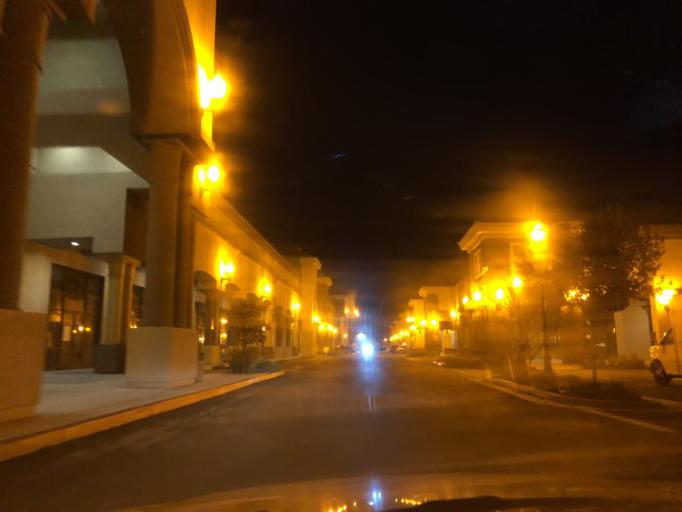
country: US
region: California
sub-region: Santa Clara County
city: San Jose
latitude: 37.3319
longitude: -121.8595
